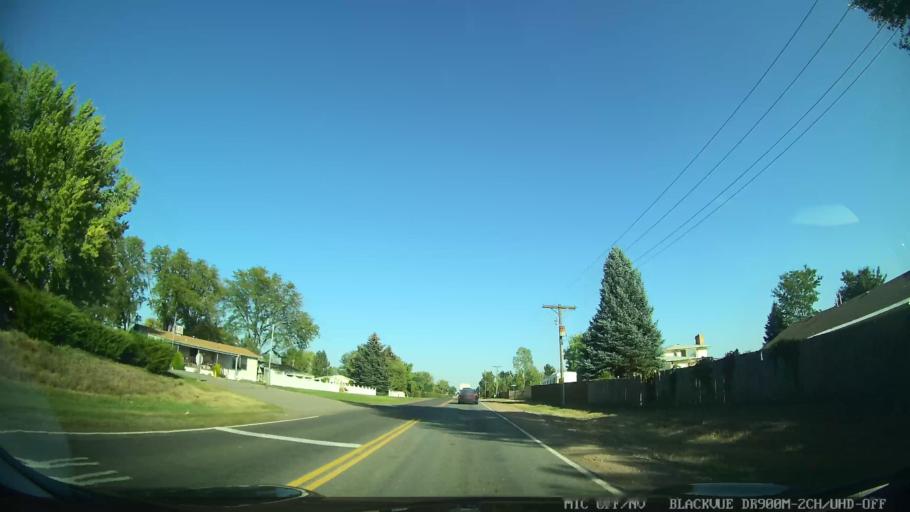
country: US
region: Colorado
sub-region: Larimer County
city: Loveland
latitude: 40.4510
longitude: -105.0867
